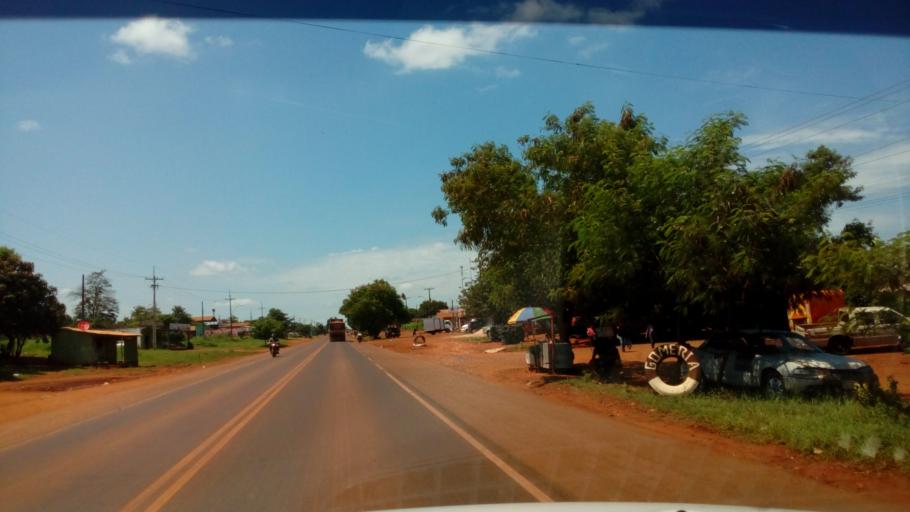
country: PY
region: Alto Parana
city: Colonia Yguazu
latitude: -25.4903
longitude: -54.8980
